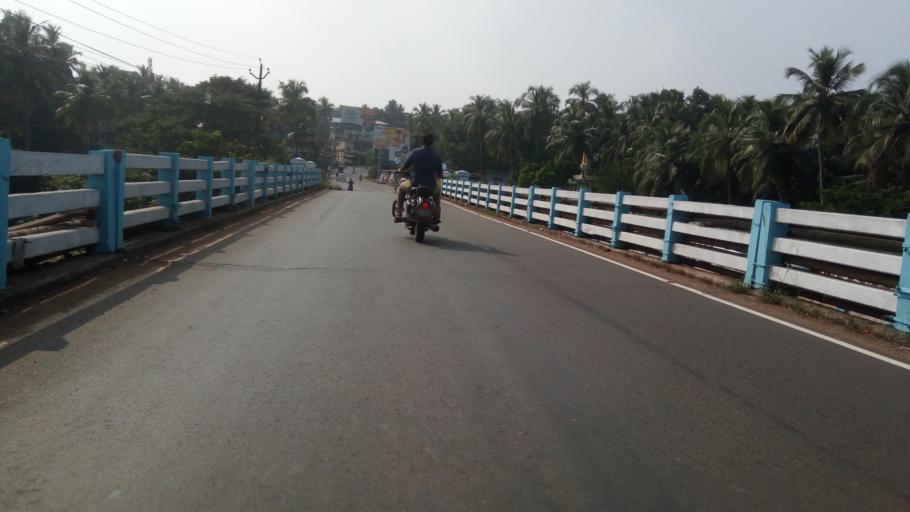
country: IN
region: Kerala
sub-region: Malappuram
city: Malappuram
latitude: 11.0036
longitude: 76.0131
